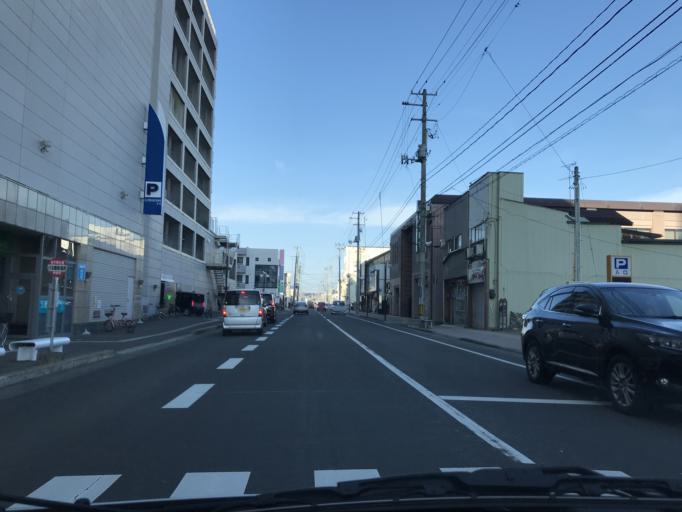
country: JP
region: Iwate
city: Kitakami
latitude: 39.2884
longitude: 141.1164
